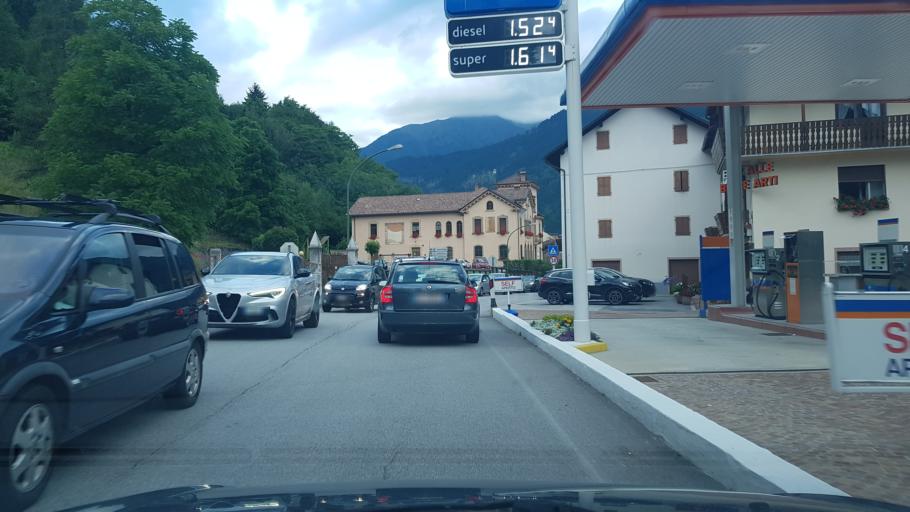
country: IT
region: Friuli Venezia Giulia
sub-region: Provincia di Udine
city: Rigolato
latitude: 46.5488
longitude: 12.8544
